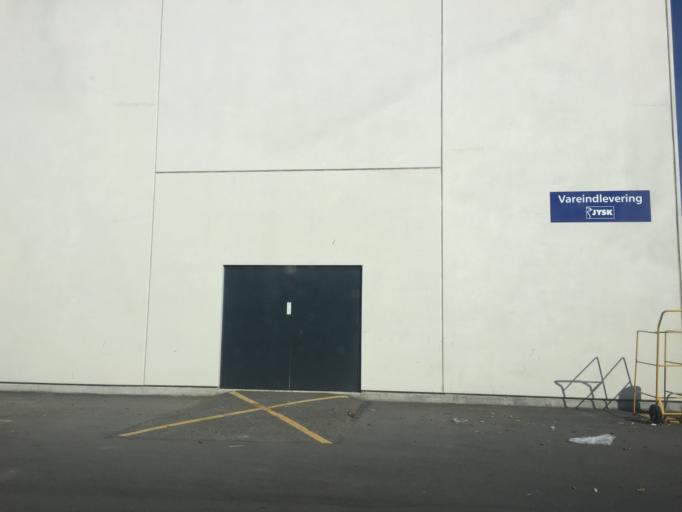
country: DK
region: Capital Region
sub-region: Albertslund Kommune
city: Albertslund
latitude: 55.6631
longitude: 12.3789
